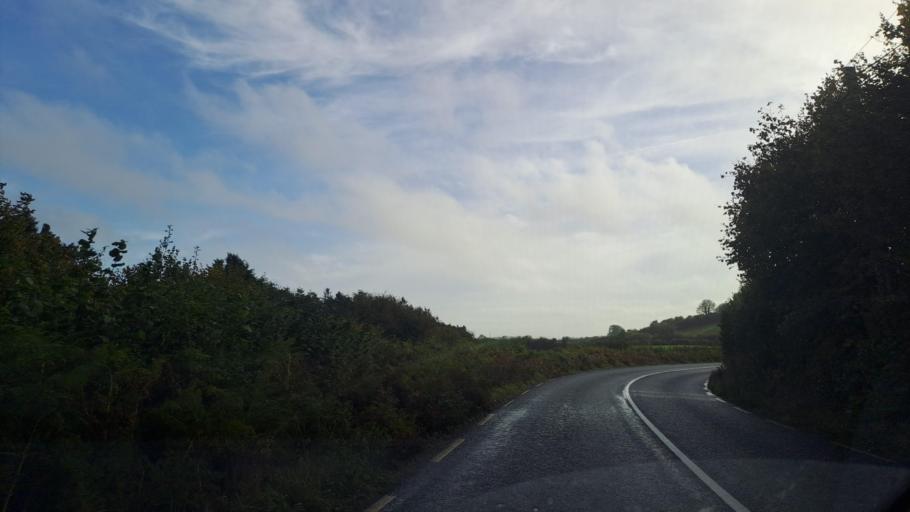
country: IE
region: Ulster
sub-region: County Monaghan
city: Carrickmacross
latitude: 53.9324
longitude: -6.7157
